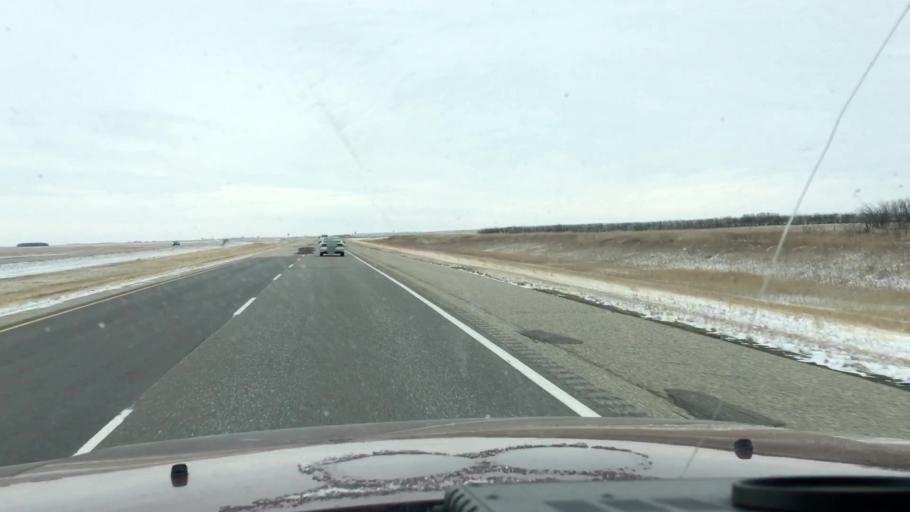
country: CA
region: Saskatchewan
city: Saskatoon
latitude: 51.4665
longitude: -106.2419
